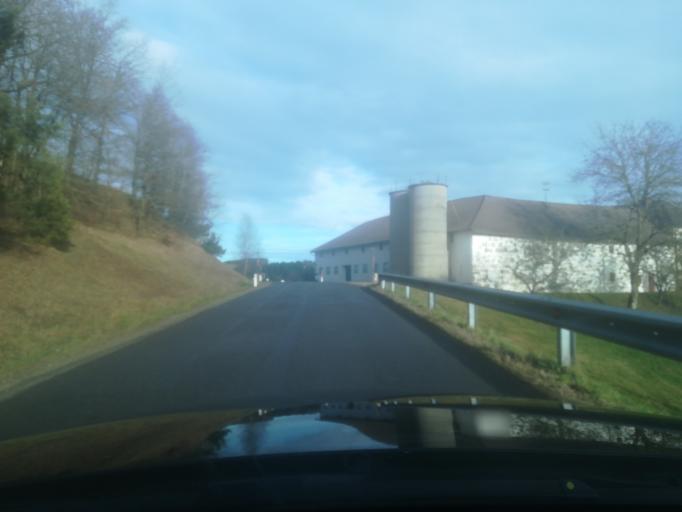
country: AT
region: Upper Austria
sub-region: Politischer Bezirk Perg
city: Perg
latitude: 48.3472
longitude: 14.6211
